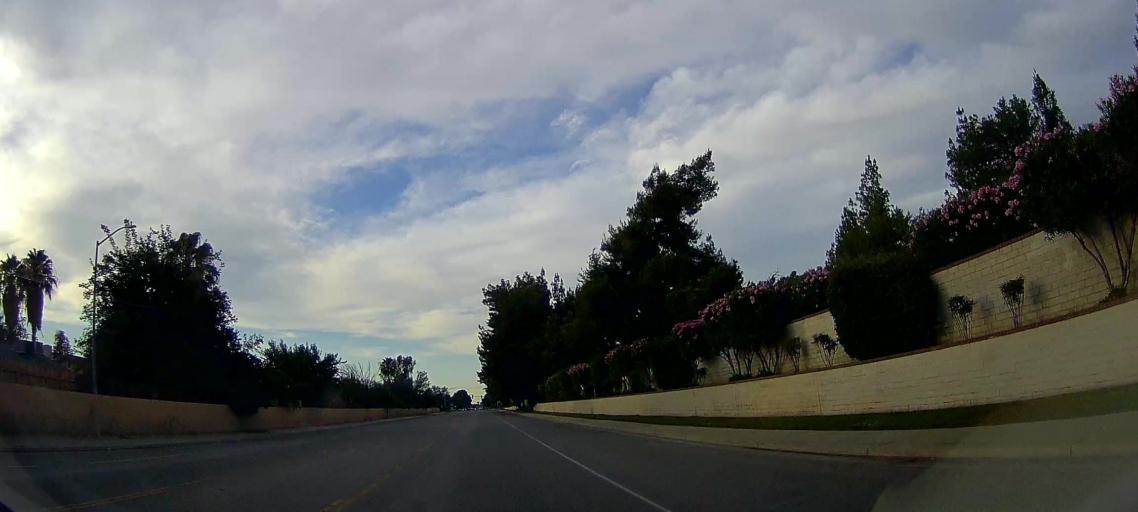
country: US
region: California
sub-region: Kern County
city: Bakersfield
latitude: 35.3224
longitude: -119.0478
